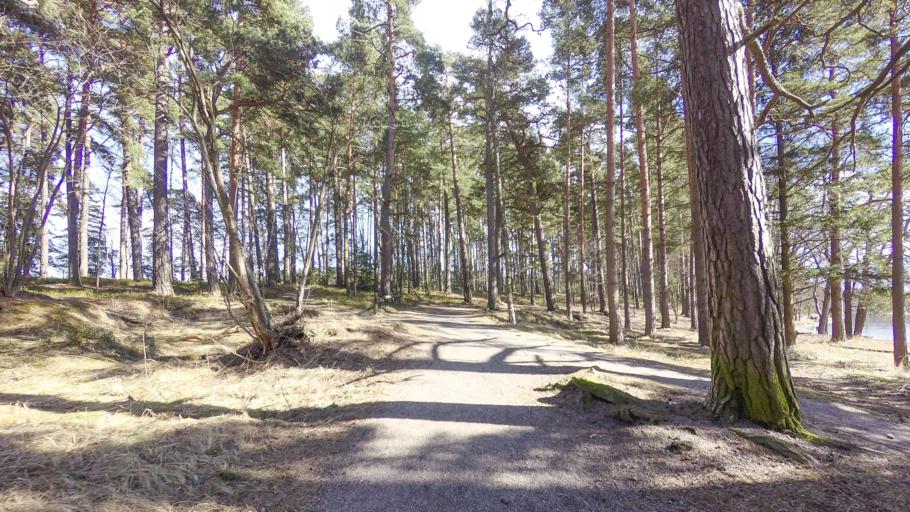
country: FI
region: Uusimaa
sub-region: Helsinki
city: Vantaa
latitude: 60.1986
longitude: 25.1321
